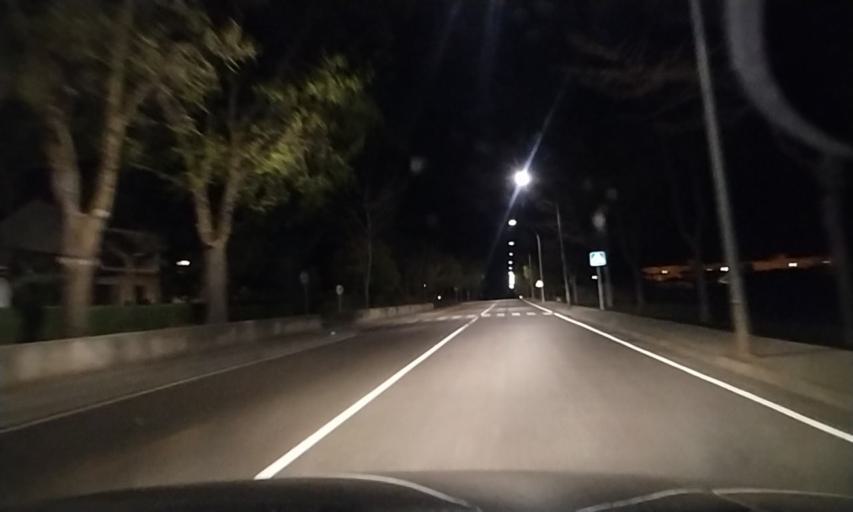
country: ES
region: Castille and Leon
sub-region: Provincia de Zamora
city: Benavente
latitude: 42.0091
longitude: -5.6864
